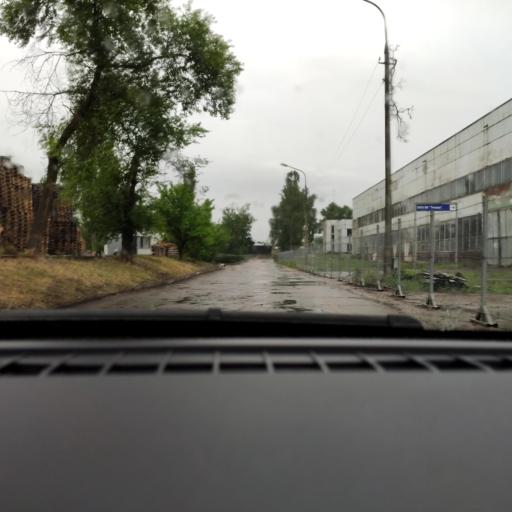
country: RU
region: Voronezj
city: Somovo
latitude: 51.7156
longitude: 39.2883
